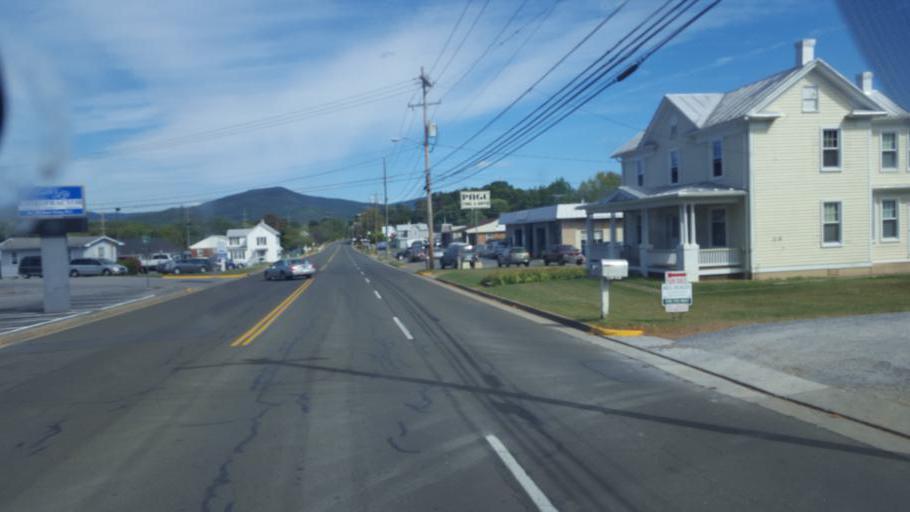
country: US
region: Virginia
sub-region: Page County
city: Luray
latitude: 38.6681
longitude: -78.4388
